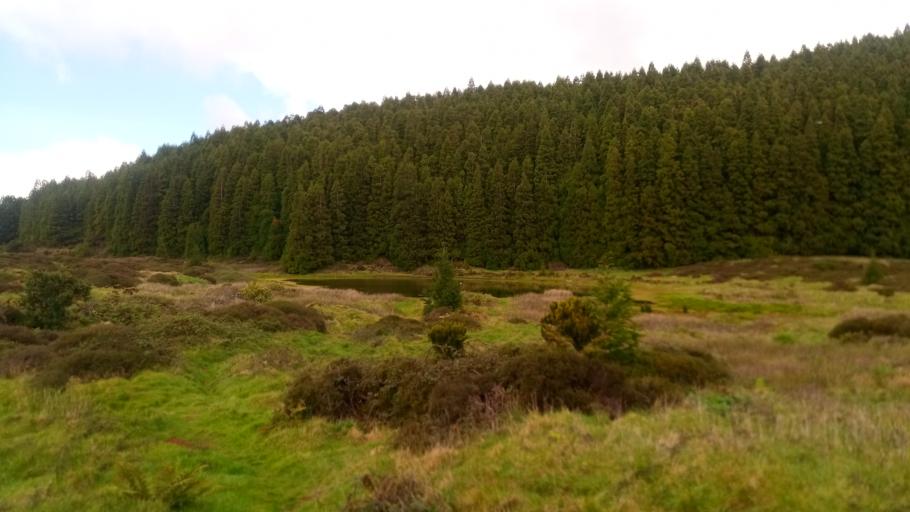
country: PT
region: Azores
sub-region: Praia da Vitoria
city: Biscoitos
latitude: 38.7373
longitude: -27.2695
